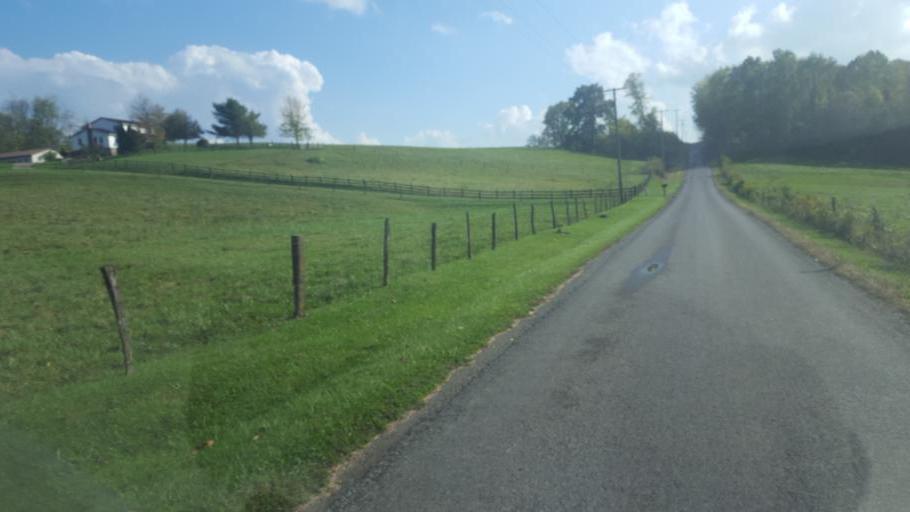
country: US
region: Ohio
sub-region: Holmes County
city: Millersburg
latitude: 40.6310
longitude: -81.8320
